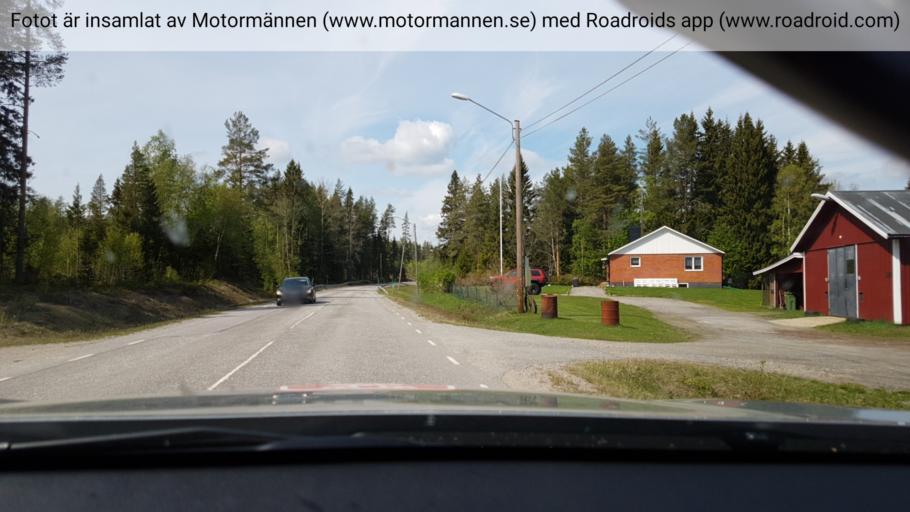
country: SE
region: Vaesterbotten
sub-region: Umea Kommun
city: Roback
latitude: 63.8569
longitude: 20.0798
